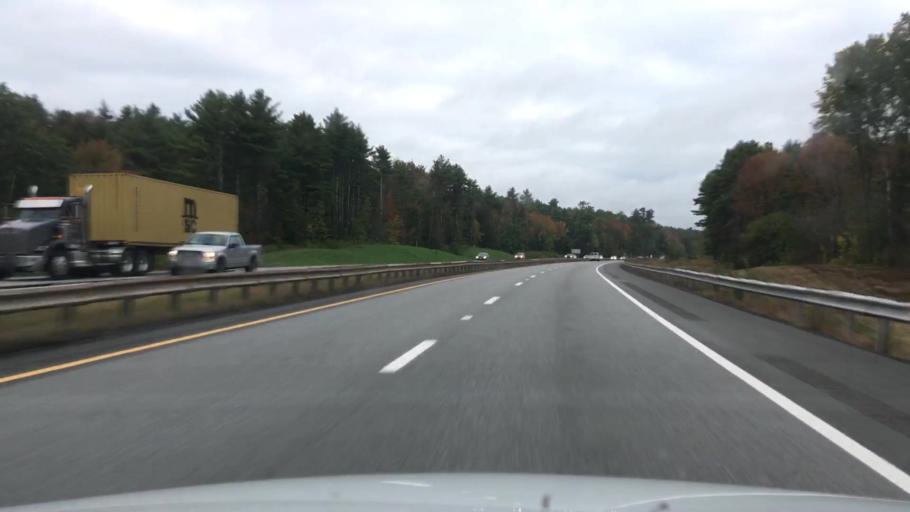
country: US
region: Maine
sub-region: Cumberland County
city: Cumberland Center
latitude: 43.7640
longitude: -70.3111
